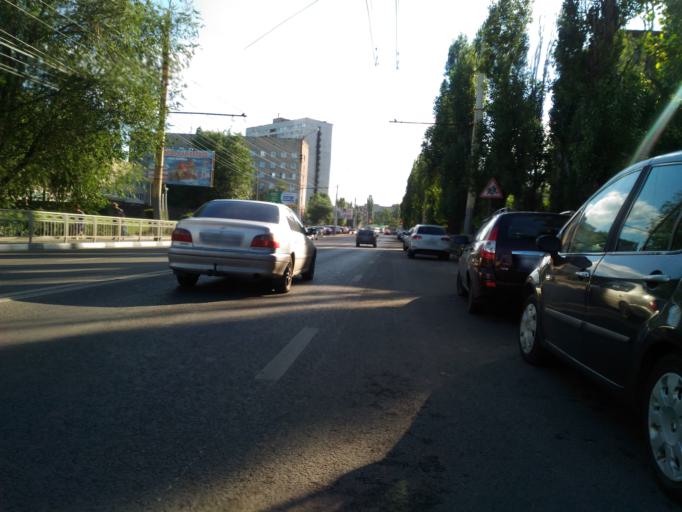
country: RU
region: Voronezj
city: Voronezh
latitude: 51.6531
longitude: 39.1467
